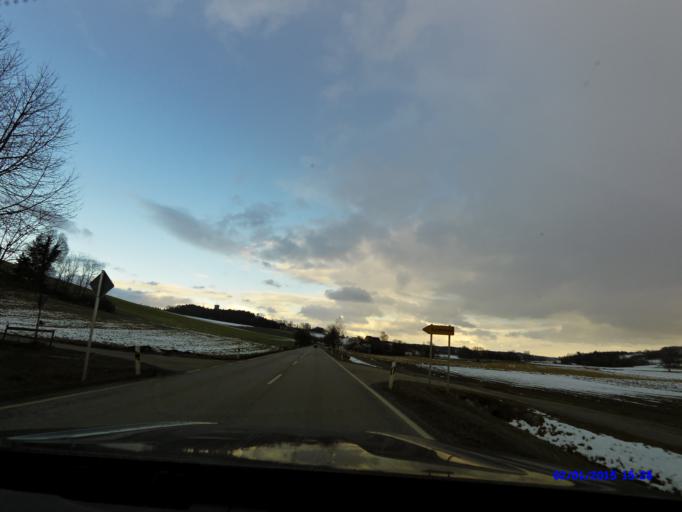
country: DE
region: Bavaria
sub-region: Lower Bavaria
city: Furth
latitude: 48.5896
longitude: 12.0306
